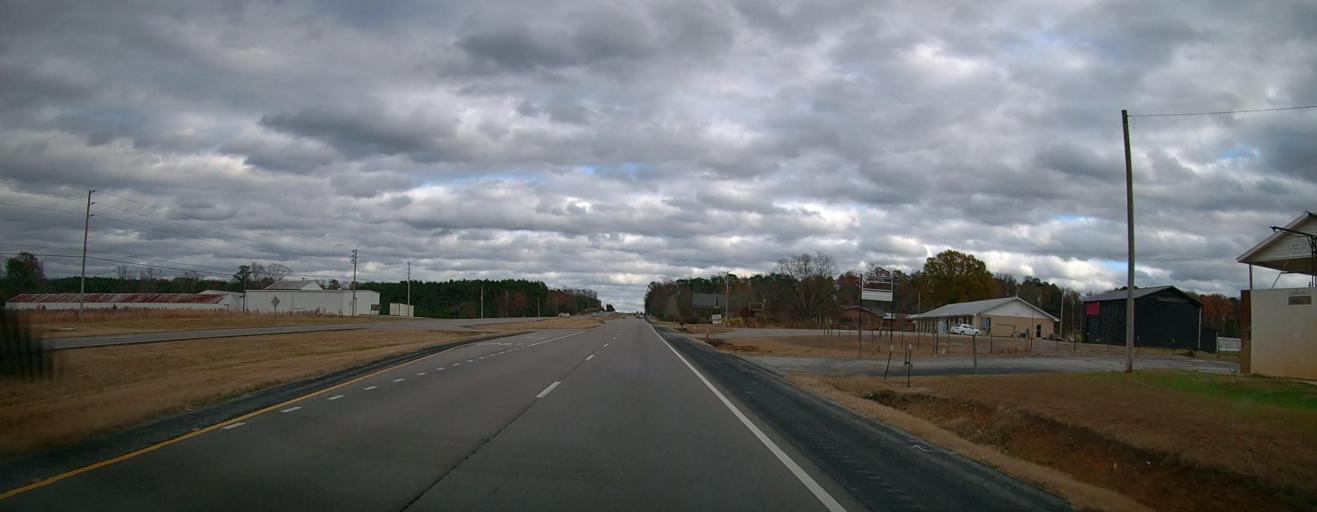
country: US
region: Alabama
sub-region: Cullman County
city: Cullman
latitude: 34.2401
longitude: -86.9520
